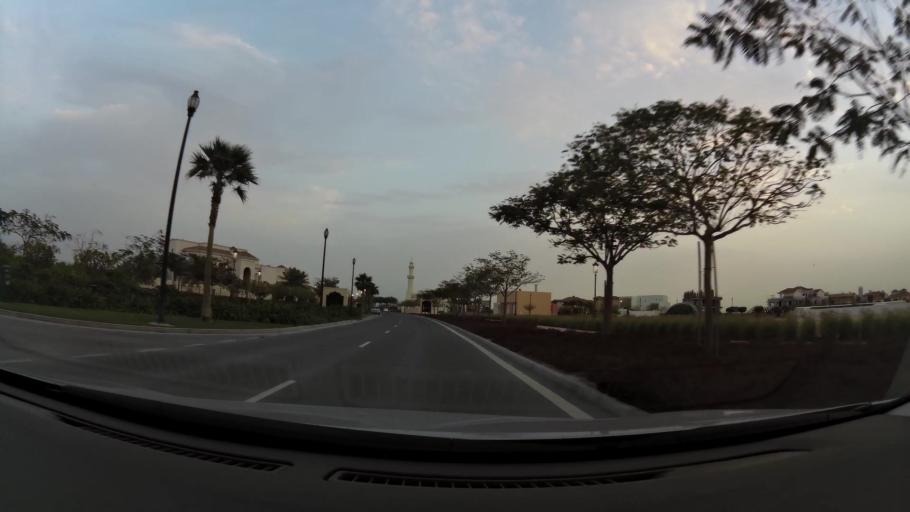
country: QA
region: Baladiyat ad Dawhah
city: Doha
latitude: 25.3639
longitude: 51.5645
